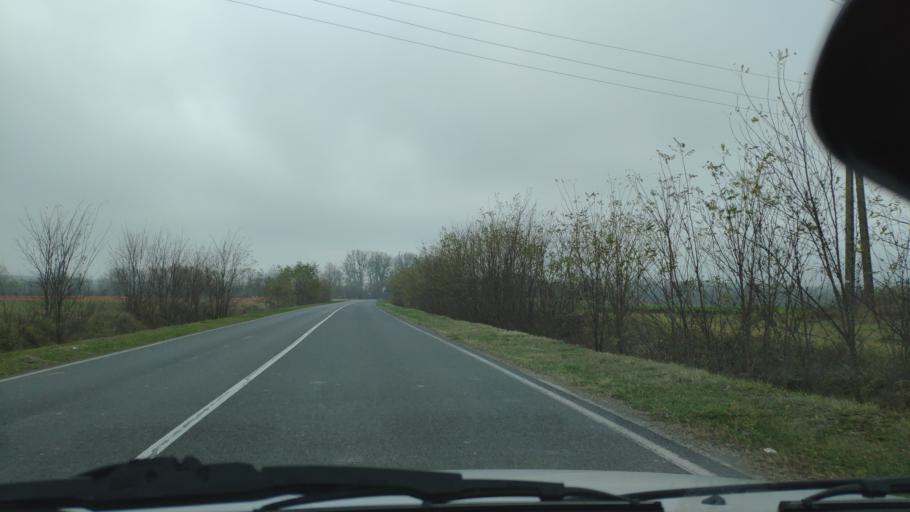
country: HU
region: Somogy
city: Balatonbereny
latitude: 46.6447
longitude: 17.2999
